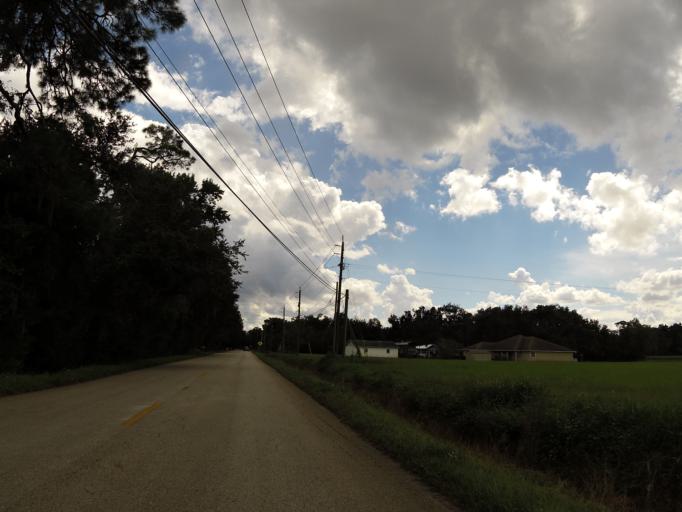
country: US
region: Florida
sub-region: Saint Johns County
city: Saint Augustine South
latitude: 29.8419
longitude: -81.4998
